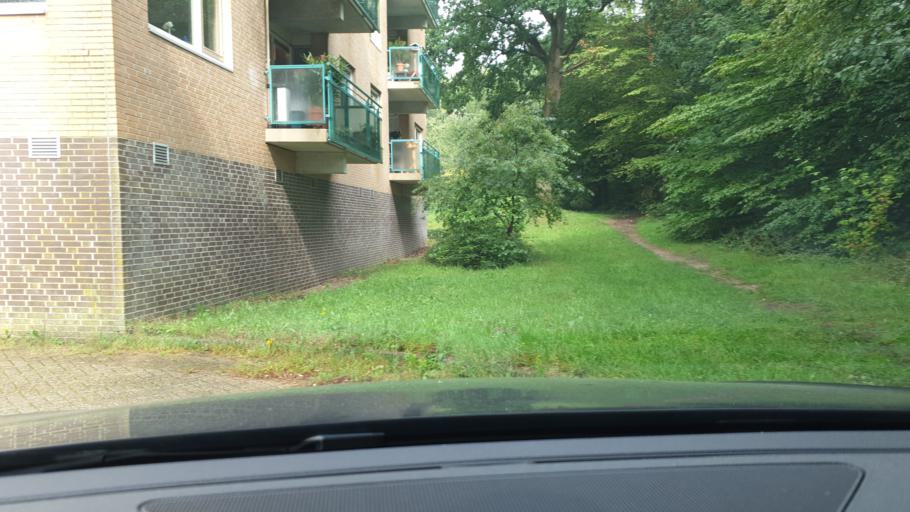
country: NL
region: Gelderland
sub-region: Gemeente Nijmegen
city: Nijmegen
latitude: 51.8166
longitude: 5.8373
